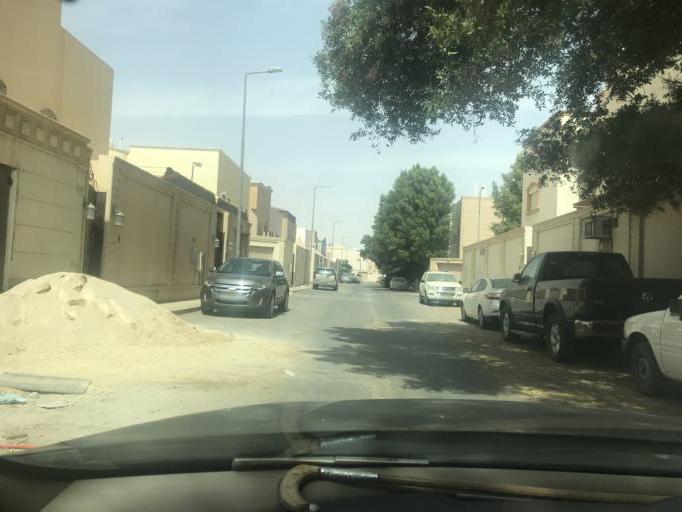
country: SA
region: Ar Riyad
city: Riyadh
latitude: 24.8019
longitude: 46.6637
